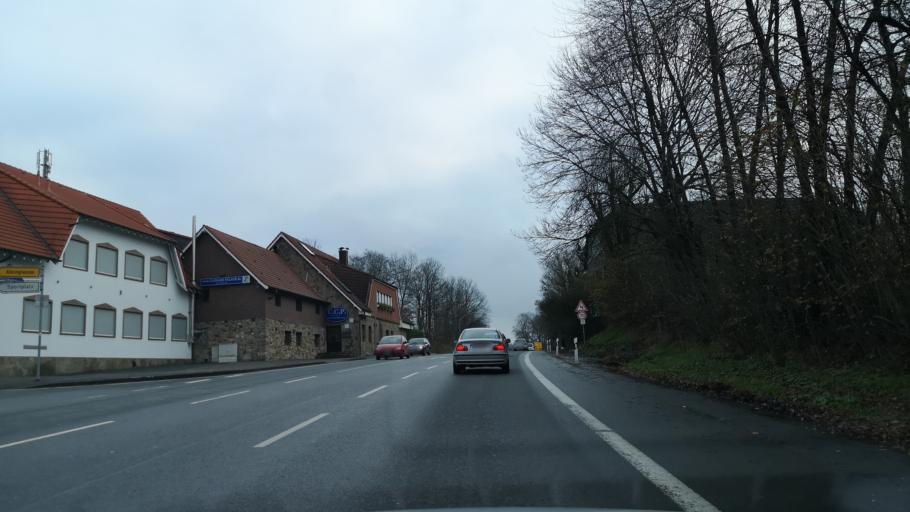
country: DE
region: North Rhine-Westphalia
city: Sprockhovel
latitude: 51.3504
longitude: 7.2909
